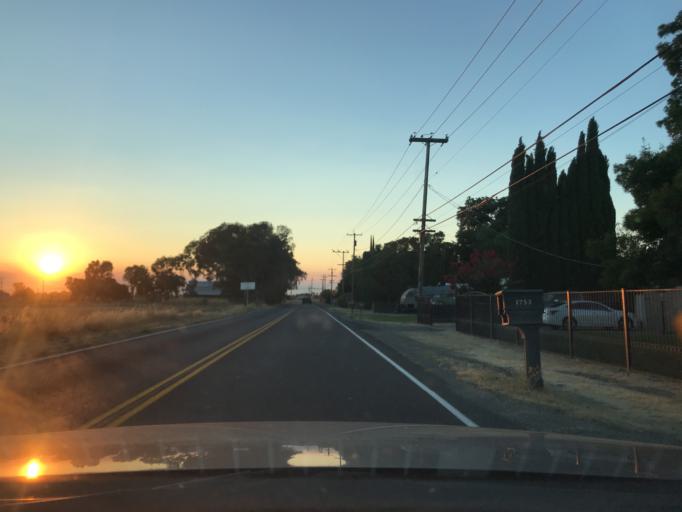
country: US
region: California
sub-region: Merced County
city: Merced
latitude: 37.3391
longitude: -120.5081
